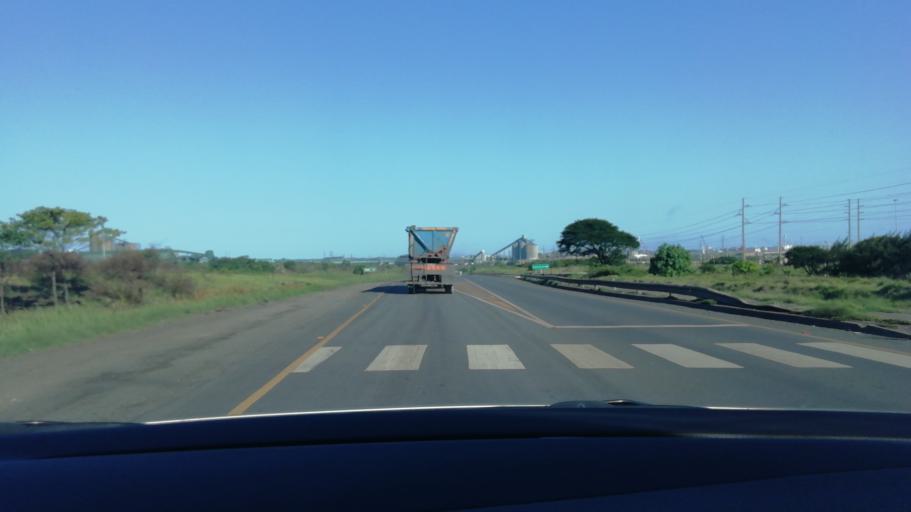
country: ZA
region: KwaZulu-Natal
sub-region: uThungulu District Municipality
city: Richards Bay
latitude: -28.7776
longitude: 32.0169
